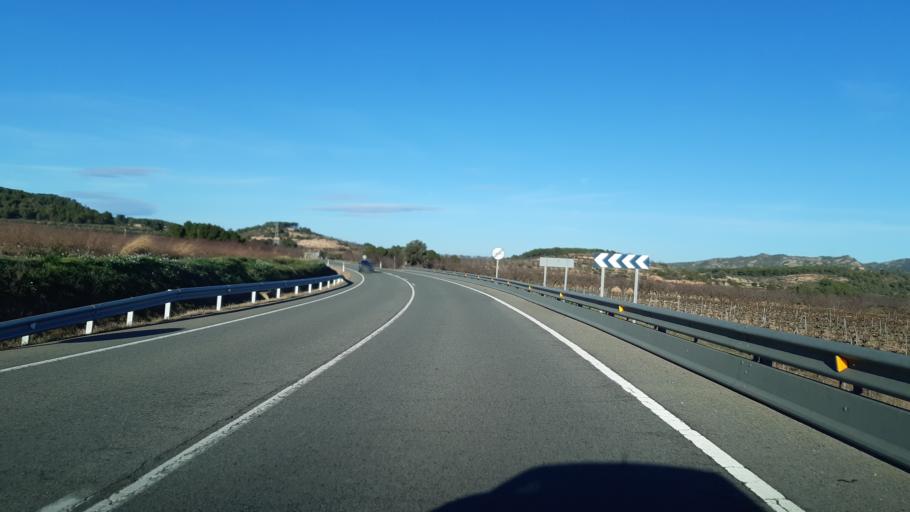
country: ES
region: Catalonia
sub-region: Provincia de Tarragona
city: la Fatarella
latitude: 41.0915
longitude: 0.5146
